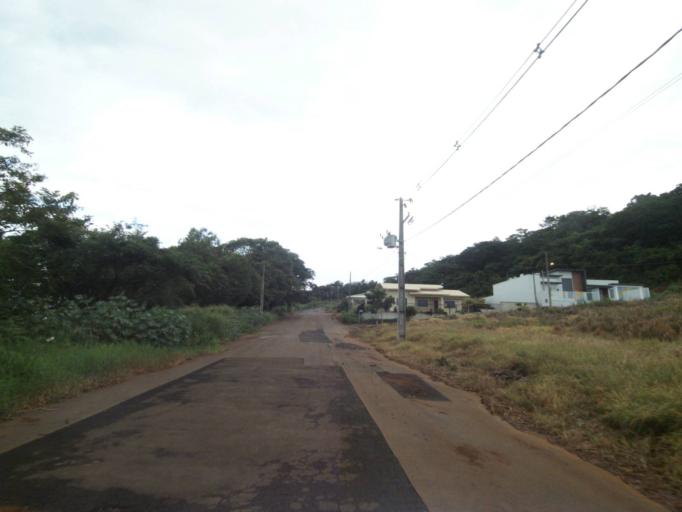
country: BR
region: Parana
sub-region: Guaraniacu
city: Guaraniacu
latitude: -25.1011
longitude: -52.8880
